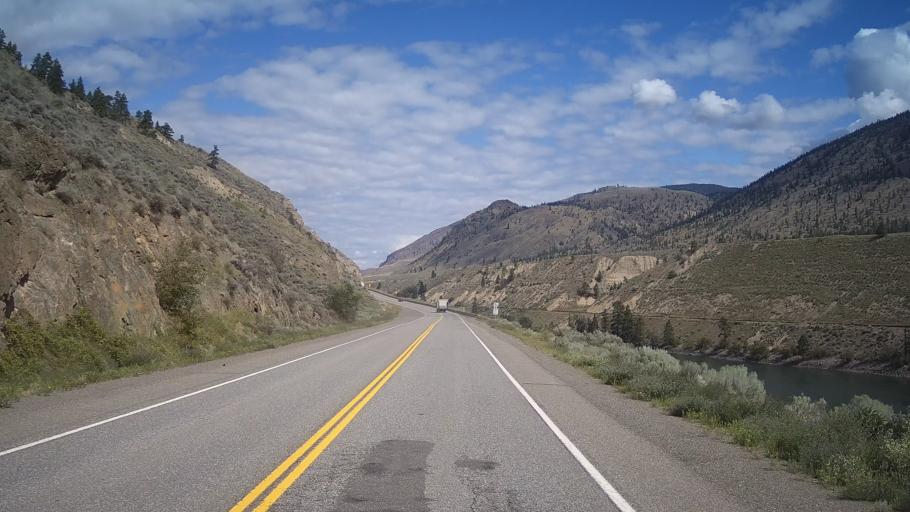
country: CA
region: British Columbia
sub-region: Thompson-Nicola Regional District
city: Ashcroft
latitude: 50.5321
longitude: -121.2857
